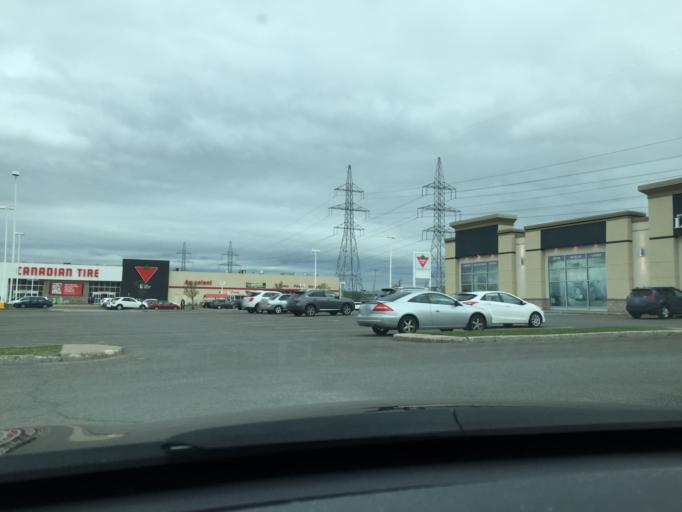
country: CA
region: Quebec
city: Quebec
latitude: 46.8413
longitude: -71.2739
